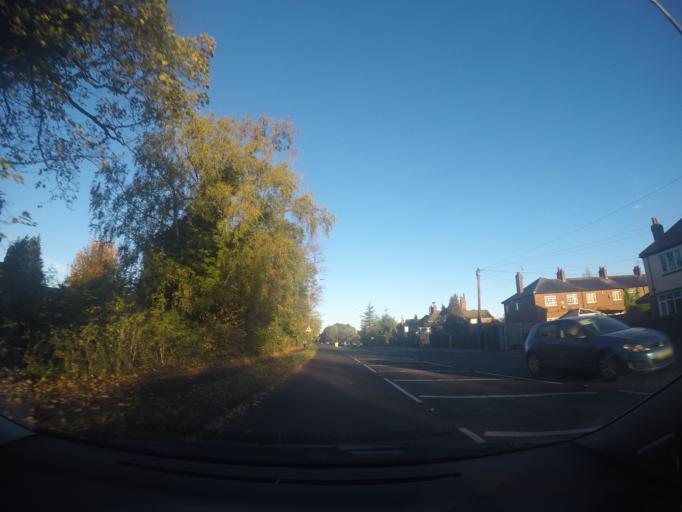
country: GB
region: England
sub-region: City of York
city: York
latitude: 53.9767
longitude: -1.1087
